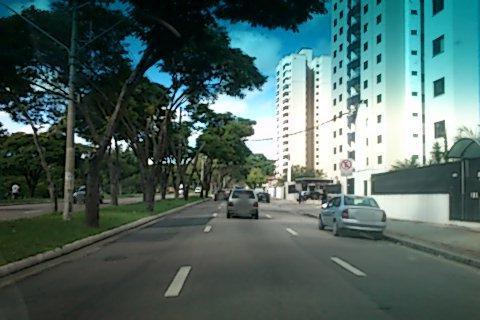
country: BR
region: Sao Paulo
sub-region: Sao Jose Dos Campos
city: Sao Jose dos Campos
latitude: -23.2378
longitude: -45.8812
